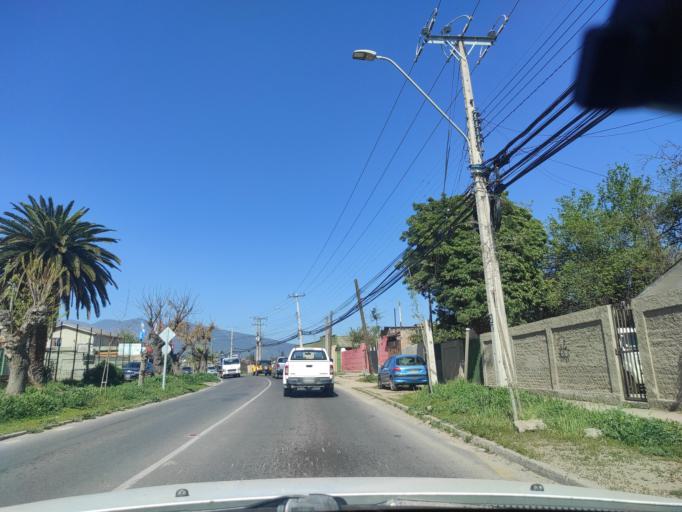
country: CL
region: Valparaiso
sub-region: Provincia de Marga Marga
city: Limache
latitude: -33.0118
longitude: -71.2529
